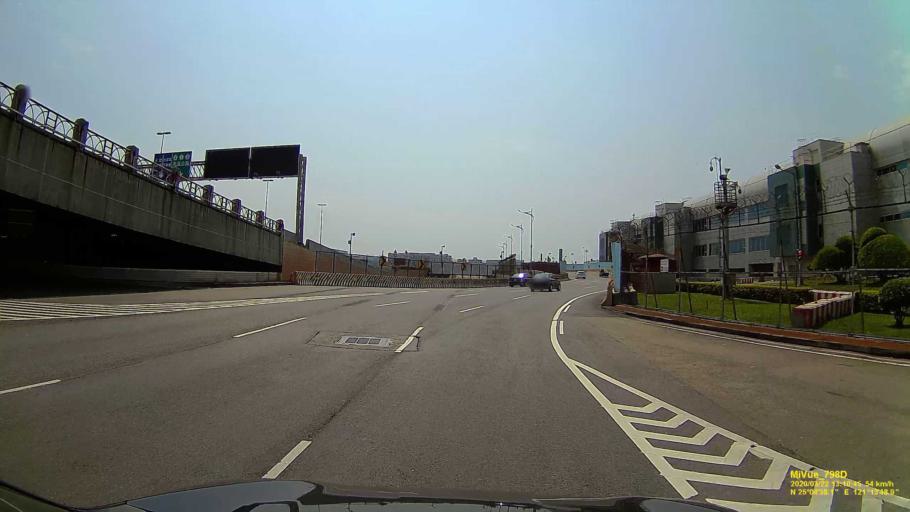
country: TW
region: Taiwan
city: Taoyuan City
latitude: 25.0774
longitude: 121.2300
